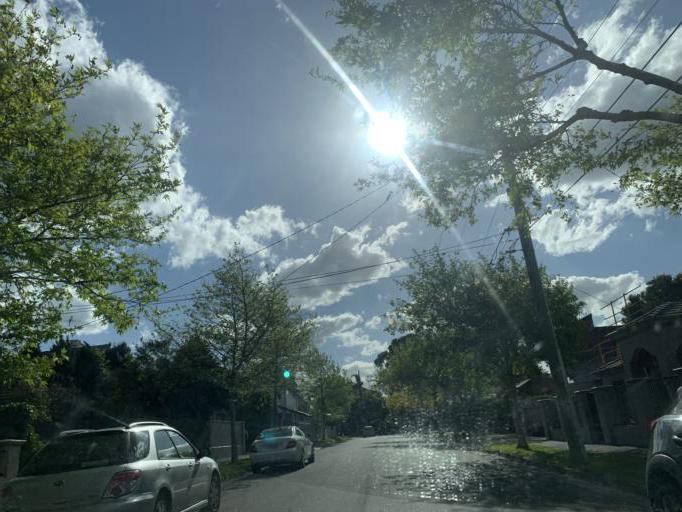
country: AU
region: Victoria
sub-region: Bayside
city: North Brighton
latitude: -37.9194
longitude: 145.0045
